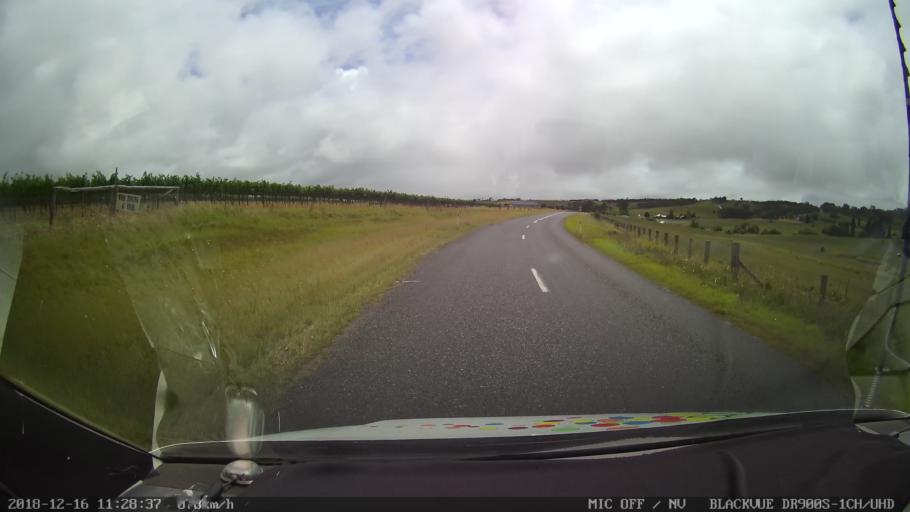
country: AU
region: New South Wales
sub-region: Tenterfield Municipality
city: Carrolls Creek
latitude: -29.0374
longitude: 152.0988
